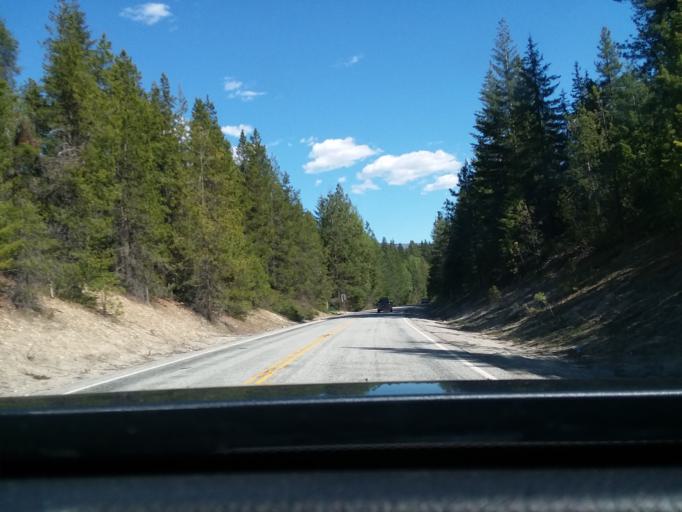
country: US
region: Washington
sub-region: Chelan County
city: Leavenworth
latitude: 47.8002
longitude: -120.6732
